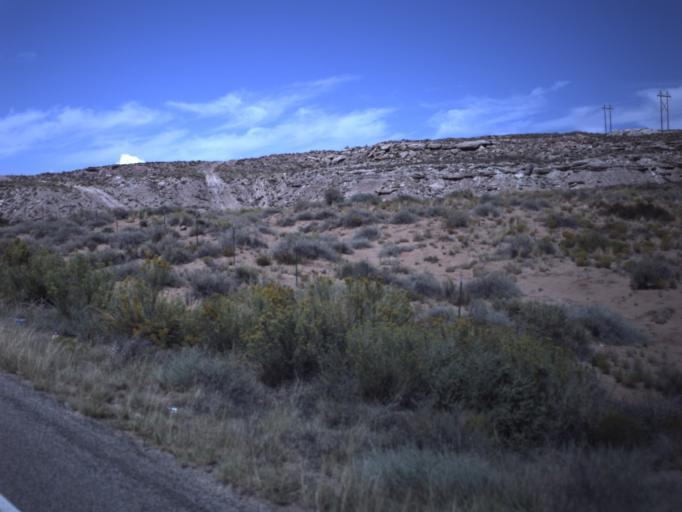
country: US
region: Utah
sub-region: San Juan County
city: Blanding
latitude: 37.2733
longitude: -109.3447
